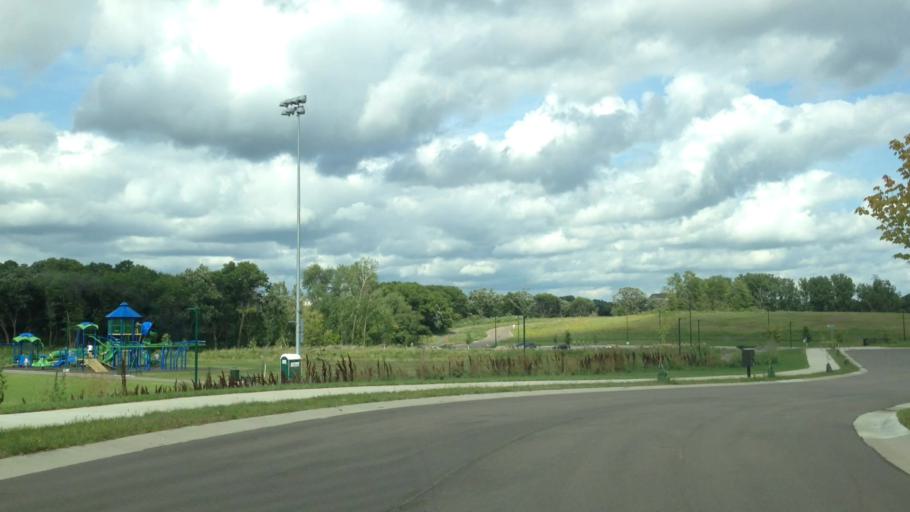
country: US
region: Minnesota
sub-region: Ramsey County
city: New Brighton
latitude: 45.0736
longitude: -93.1962
